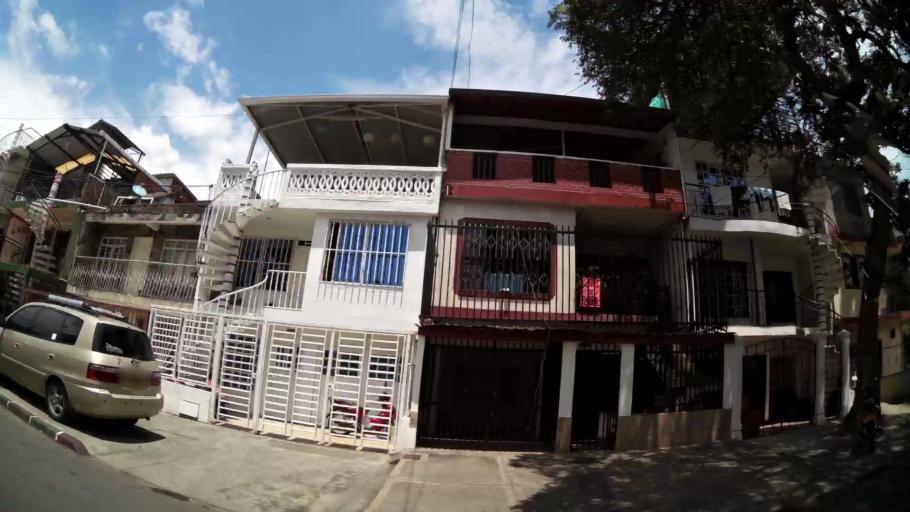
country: CO
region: Valle del Cauca
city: Cali
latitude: 3.4411
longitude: -76.5047
